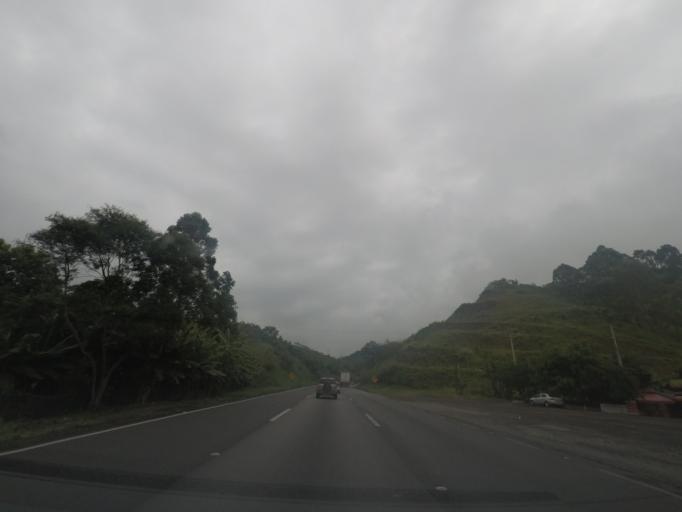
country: BR
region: Sao Paulo
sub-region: Cajati
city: Cajati
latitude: -24.8555
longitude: -48.2162
